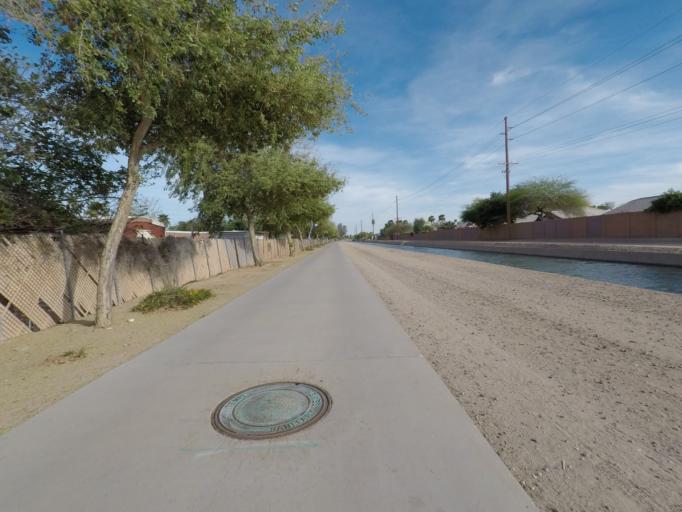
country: US
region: Arizona
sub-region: Maricopa County
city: Guadalupe
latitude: 33.3807
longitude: -111.9478
